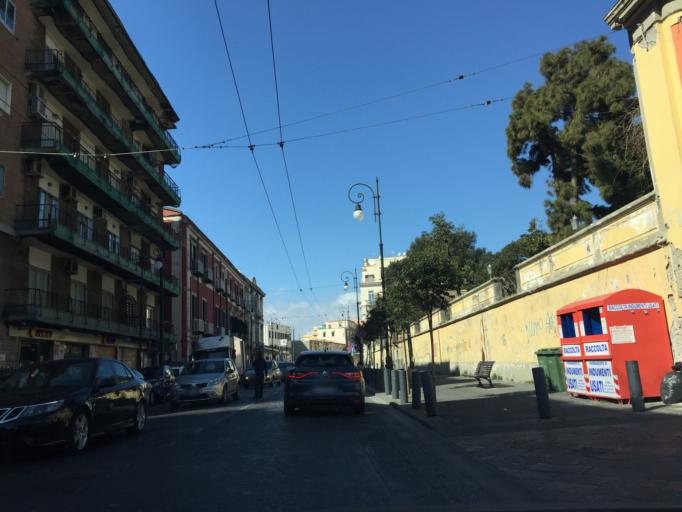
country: IT
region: Campania
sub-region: Provincia di Napoli
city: Portici
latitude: 40.8182
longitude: 14.3305
